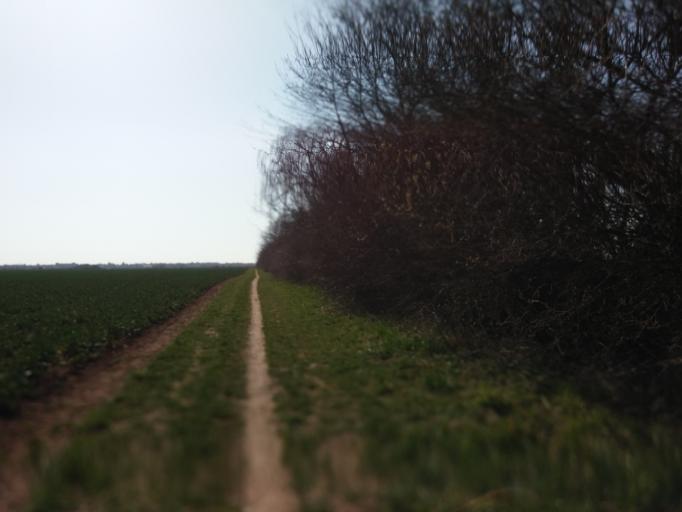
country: DE
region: Bavaria
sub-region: Upper Bavaria
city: Haar
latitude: 48.1225
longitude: 11.7293
